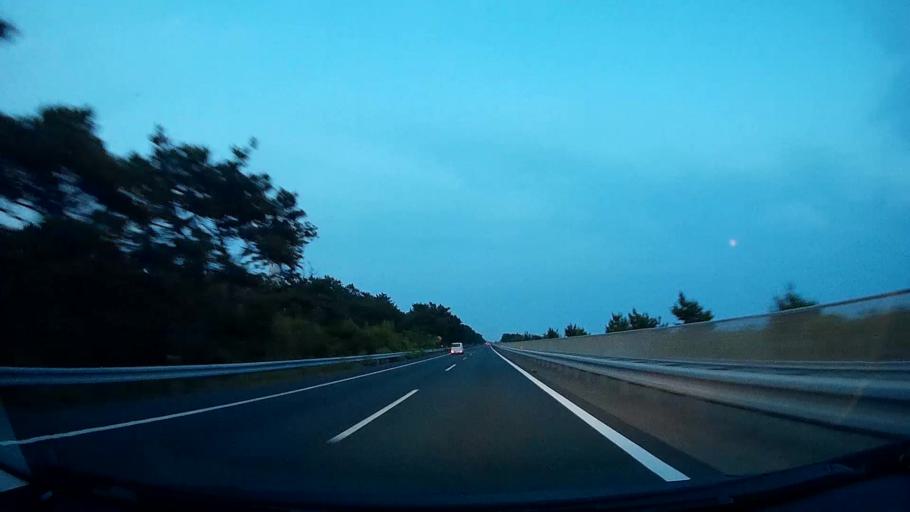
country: JP
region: Shizuoka
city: Kosai-shi
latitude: 34.6783
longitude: 137.6113
